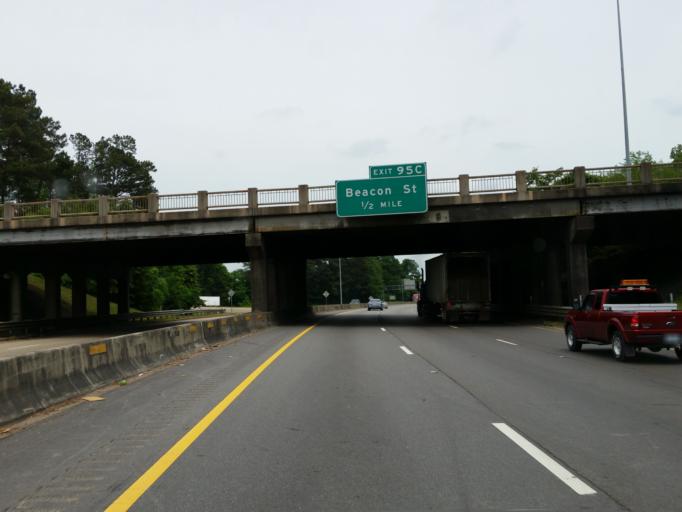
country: US
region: Mississippi
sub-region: Jones County
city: Laurel
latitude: 31.6842
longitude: -89.1472
